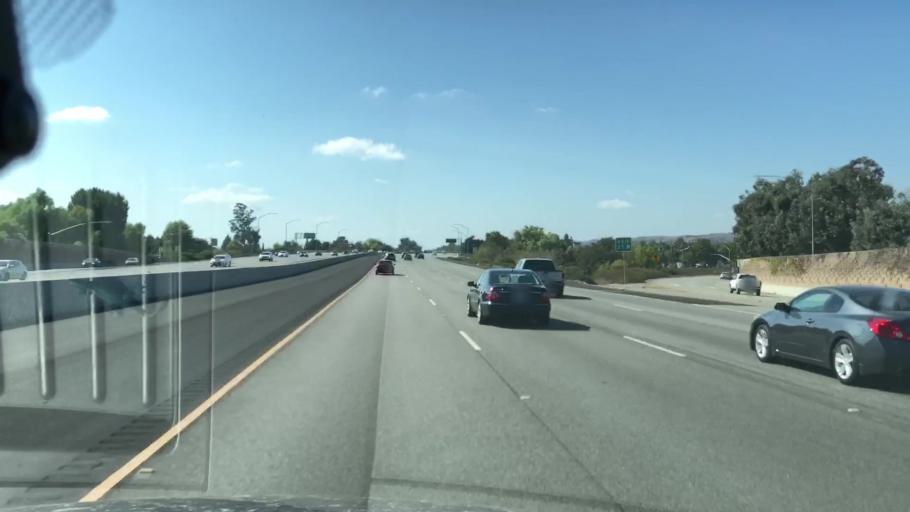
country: US
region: California
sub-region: Ventura County
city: Santa Susana
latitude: 34.2819
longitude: -118.7141
